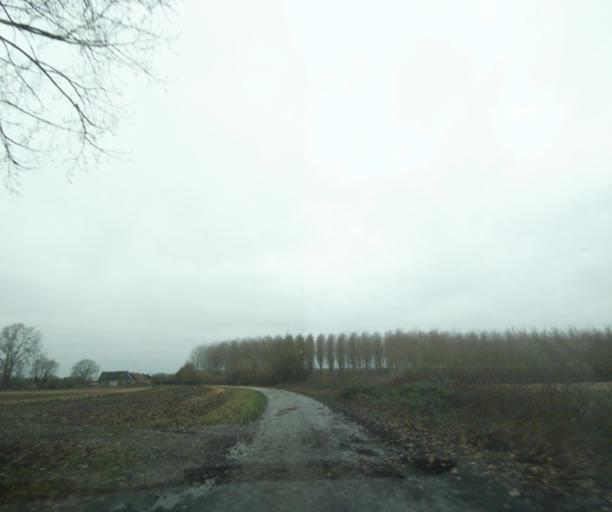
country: FR
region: Nord-Pas-de-Calais
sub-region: Departement du Nord
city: Vicq
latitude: 50.4251
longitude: 3.6075
